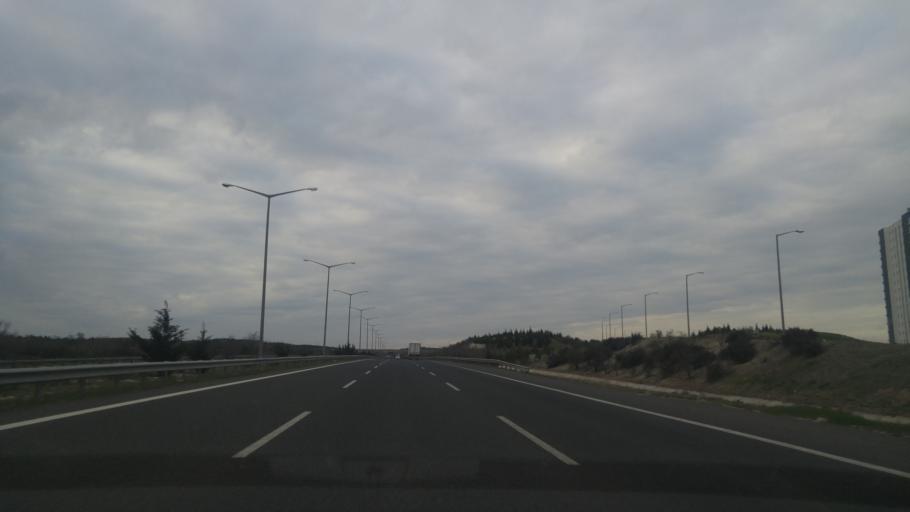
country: TR
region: Ankara
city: Etimesgut
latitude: 40.0085
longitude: 32.6314
